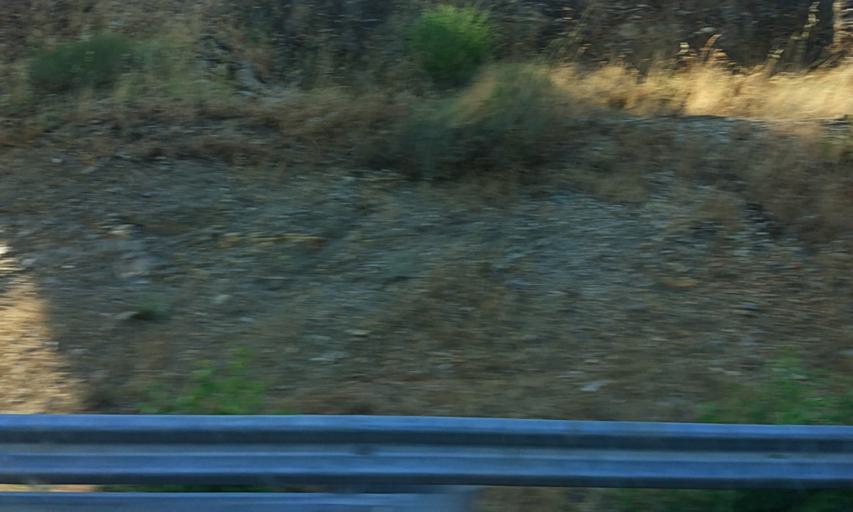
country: PT
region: Braganca
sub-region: Mirandela
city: Mirandela
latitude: 41.5199
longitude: -7.1302
